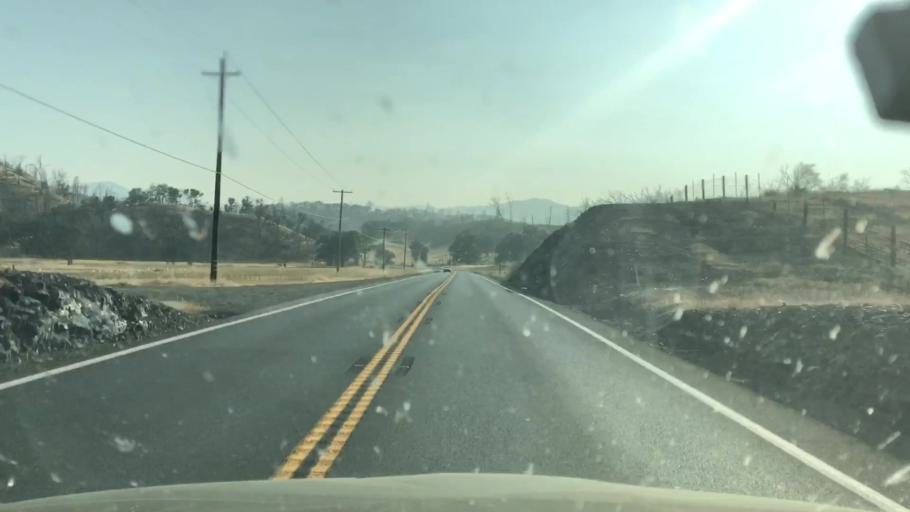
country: US
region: California
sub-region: Lake County
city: Hidden Valley Lake
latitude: 38.7760
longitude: -122.5796
